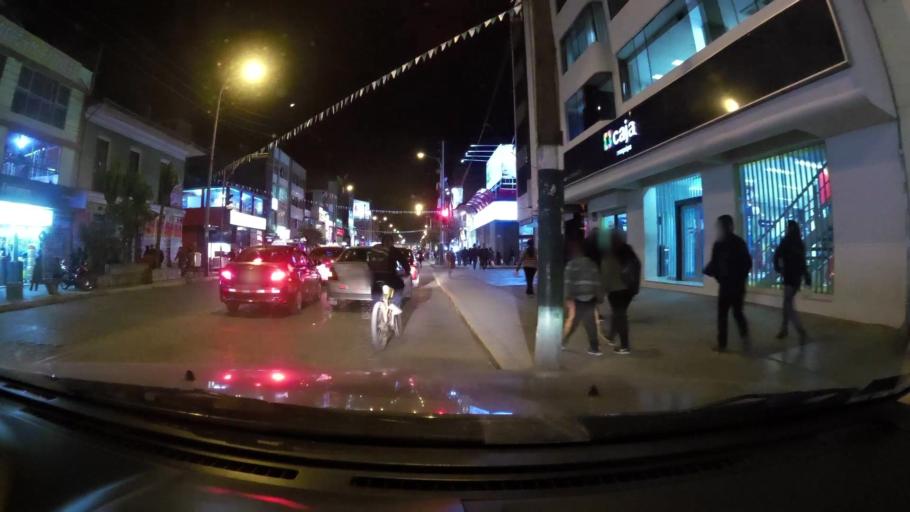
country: PE
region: Junin
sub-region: Provincia de Huancayo
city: Huancayo
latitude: -12.0736
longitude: -75.2073
